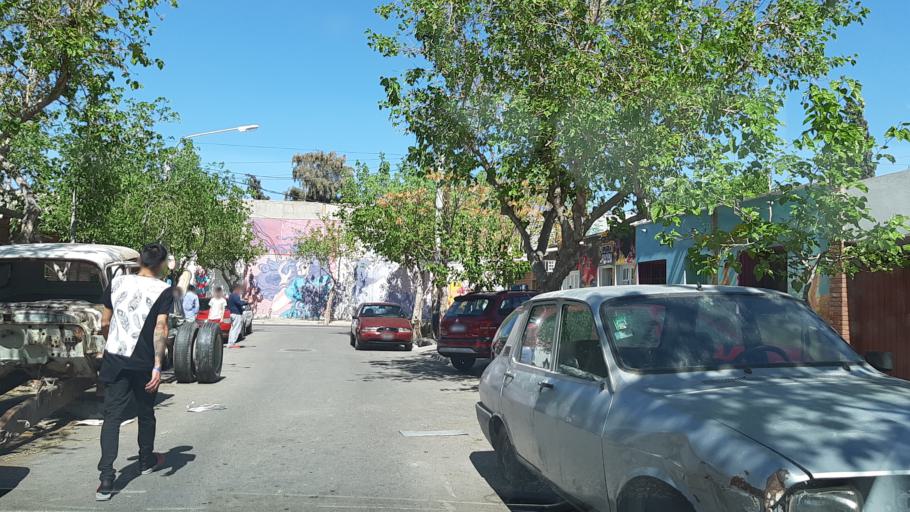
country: AR
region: San Juan
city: San Juan
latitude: -31.5257
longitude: -68.5403
